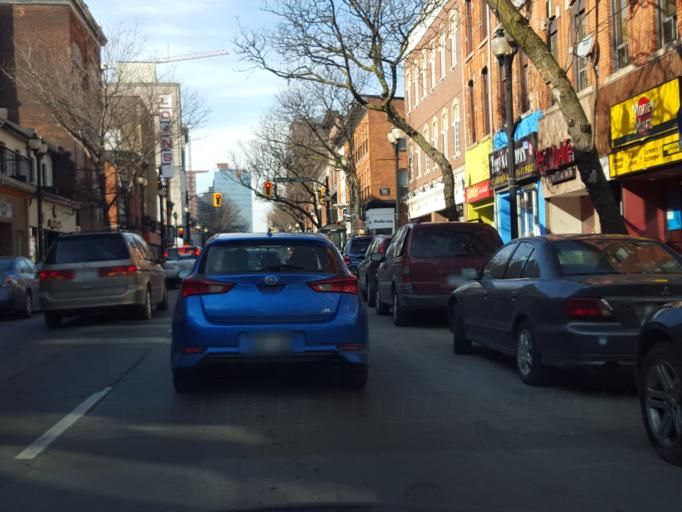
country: CA
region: Ontario
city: Hamilton
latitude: 43.2546
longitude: -79.8625
